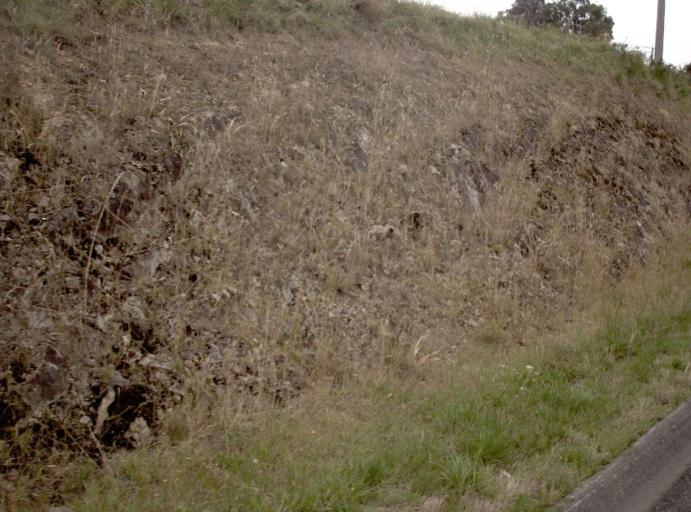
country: AU
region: Victoria
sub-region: Yarra Ranges
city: Yarra Glen
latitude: -37.5797
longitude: 145.4129
